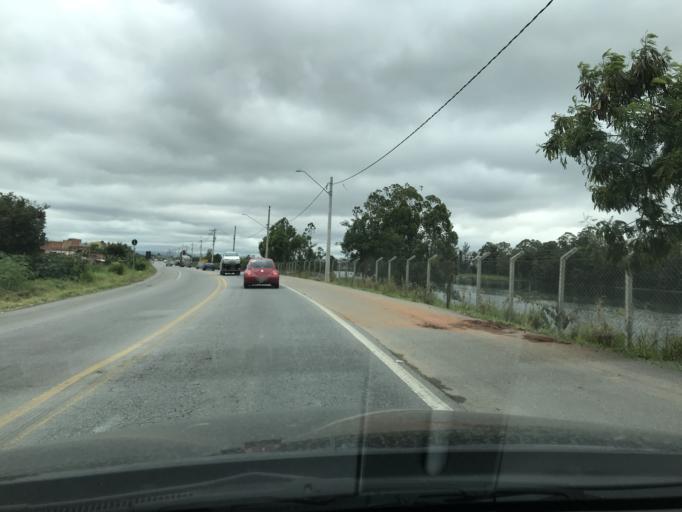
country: BR
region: Sao Paulo
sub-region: Itaquaquecetuba
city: Itaquaquecetuba
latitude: -23.4897
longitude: -46.3275
